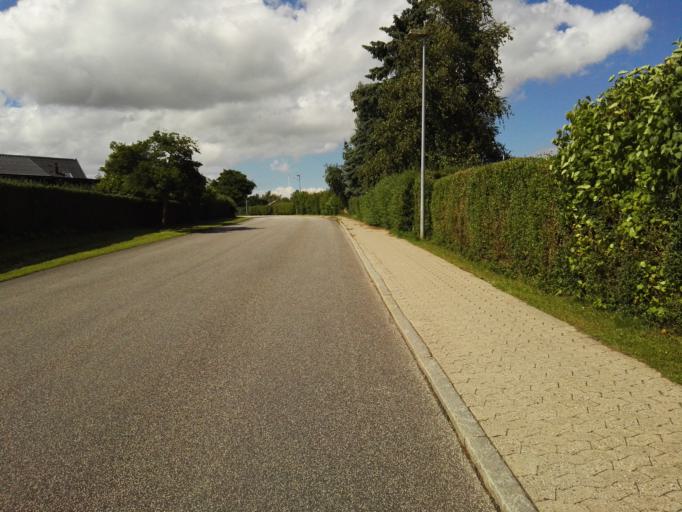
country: DK
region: Capital Region
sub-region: Egedal Kommune
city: Stenlose
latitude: 55.7965
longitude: 12.2245
